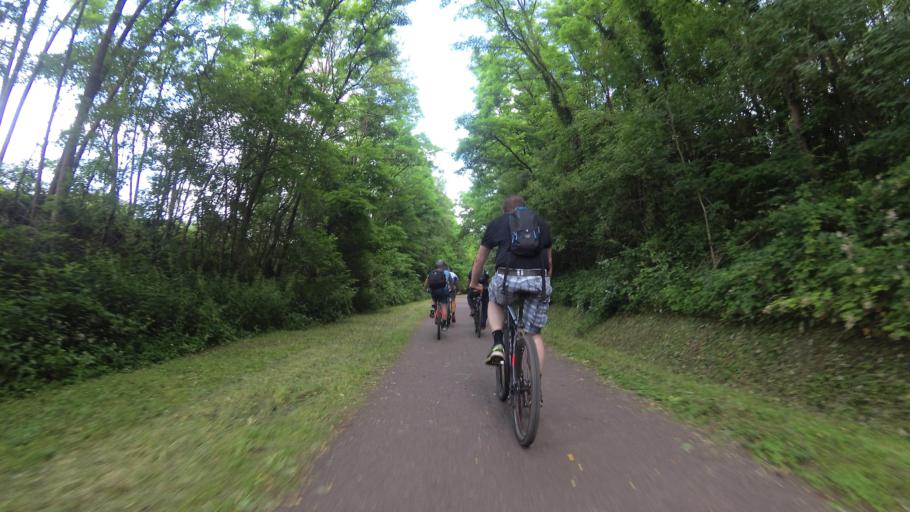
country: FR
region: Lorraine
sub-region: Departement de la Moselle
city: Sarreinsming
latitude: 49.1214
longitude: 7.1299
